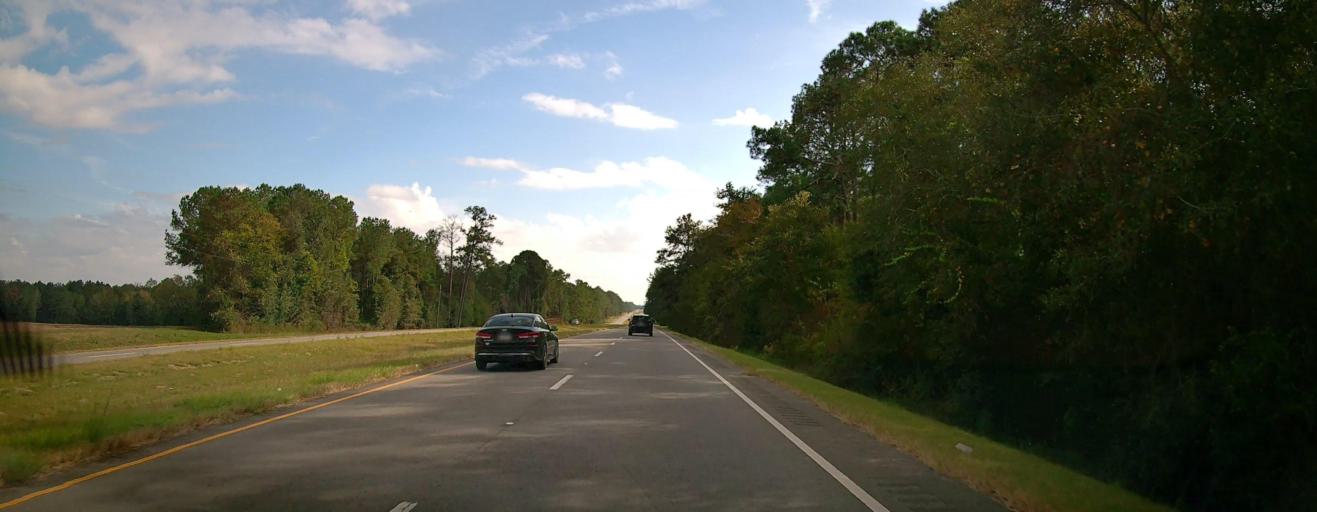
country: US
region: Georgia
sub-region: Thomas County
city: Meigs
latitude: 30.9745
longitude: -84.0360
